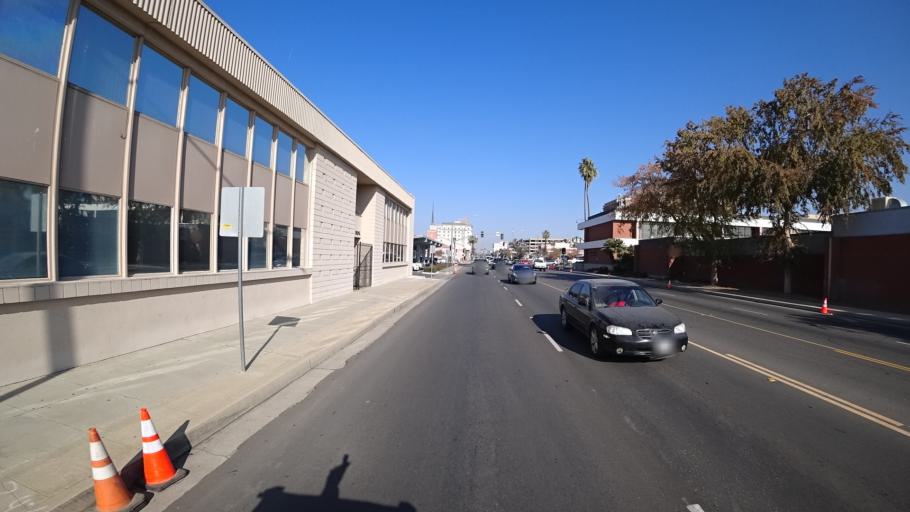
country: US
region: California
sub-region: Kern County
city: Bakersfield
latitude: 35.3725
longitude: -119.0213
